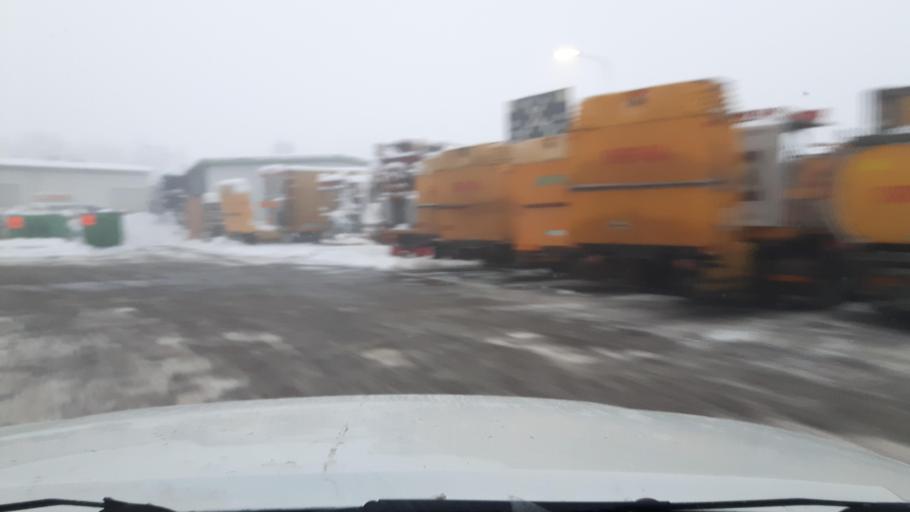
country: SE
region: Vaestra Goetaland
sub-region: Goteborg
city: Goeteborg
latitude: 57.7450
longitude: 11.9437
